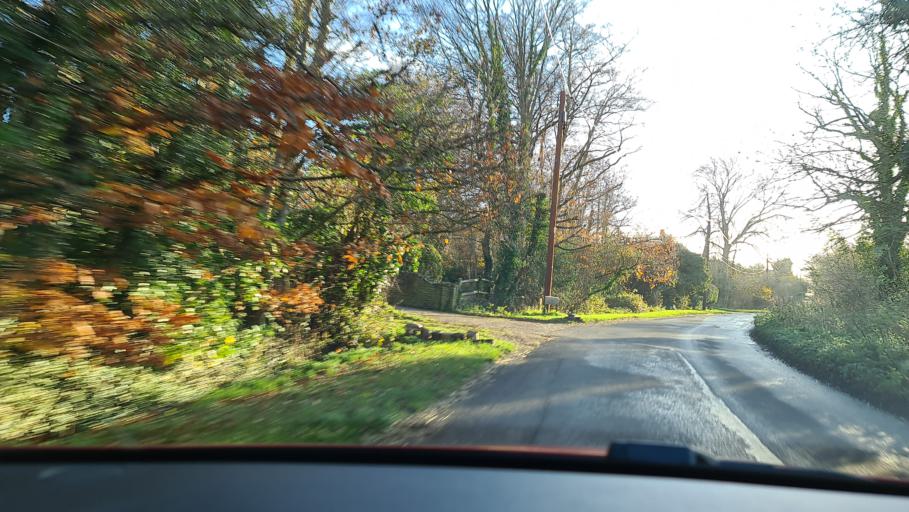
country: GB
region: England
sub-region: Buckinghamshire
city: Weston Turville
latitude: 51.7715
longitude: -0.7922
